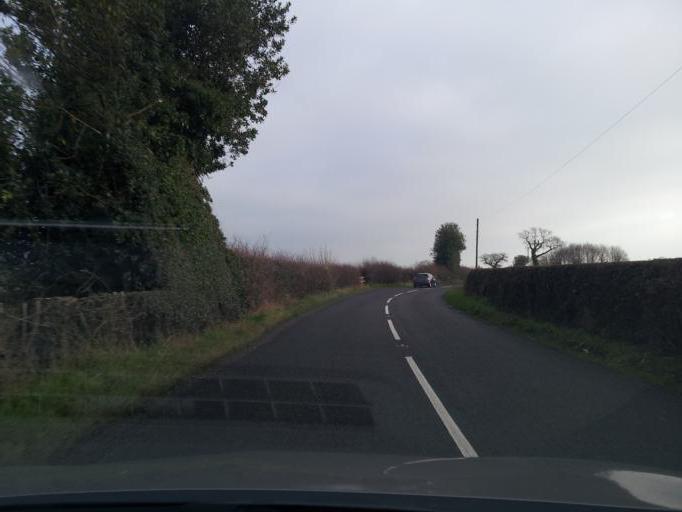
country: GB
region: England
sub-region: Derbyshire
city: Rodsley
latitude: 52.8801
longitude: -1.7491
